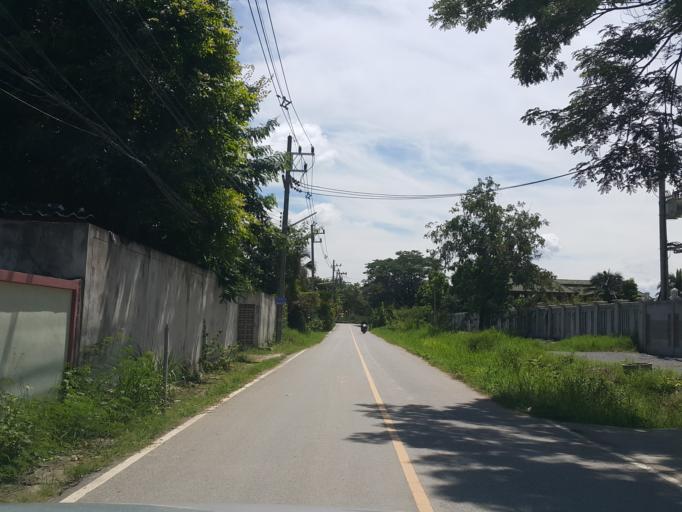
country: TH
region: Chiang Mai
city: Chiang Mai
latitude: 18.7454
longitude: 98.9474
